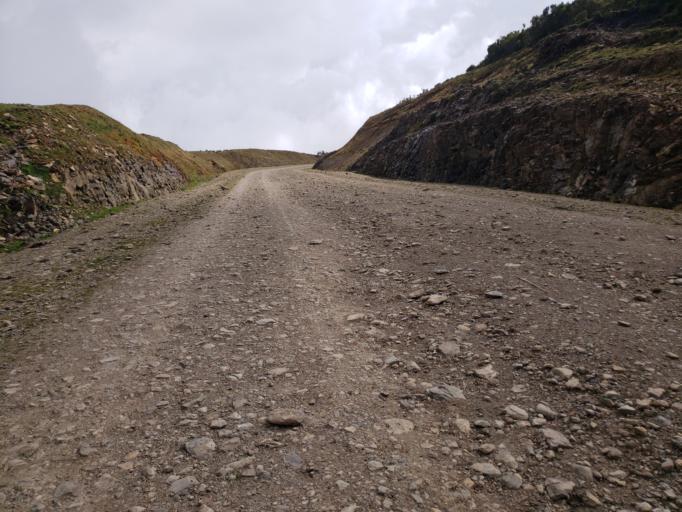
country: ET
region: Oromiya
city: Dodola
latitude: 6.7521
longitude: 39.4285
